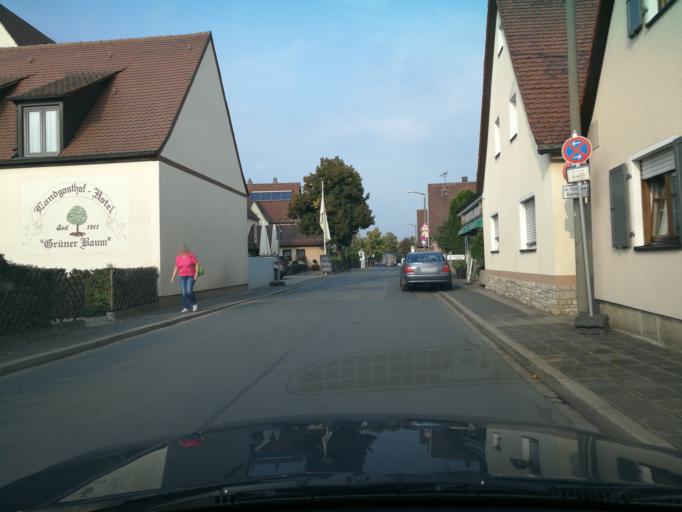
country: DE
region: Bavaria
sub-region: Regierungsbezirk Mittelfranken
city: Wetzendorf
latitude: 49.5192
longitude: 11.0501
